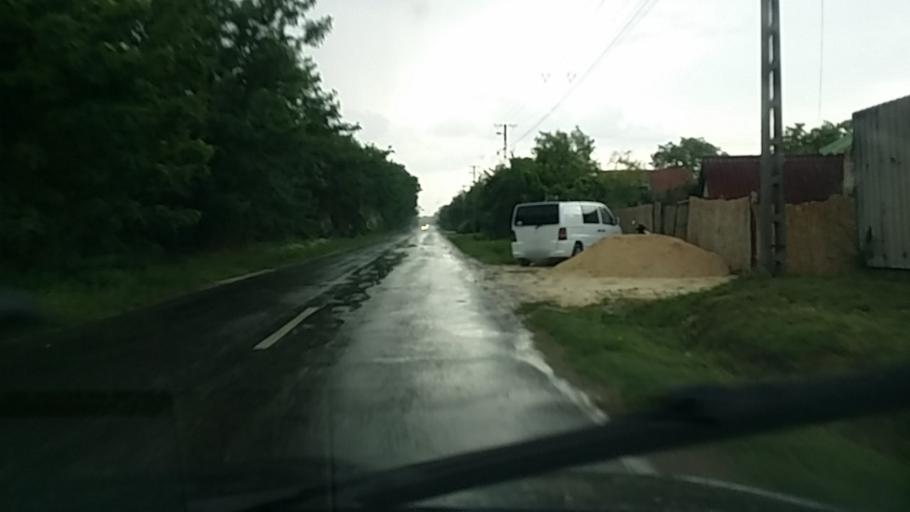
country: HU
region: Pest
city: Ocsa
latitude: 47.2919
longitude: 19.2502
